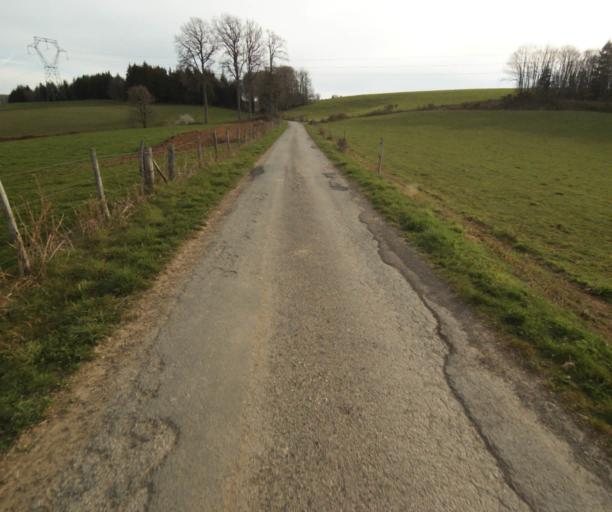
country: FR
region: Limousin
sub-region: Departement de la Correze
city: Chamboulive
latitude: 45.4628
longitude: 1.7643
